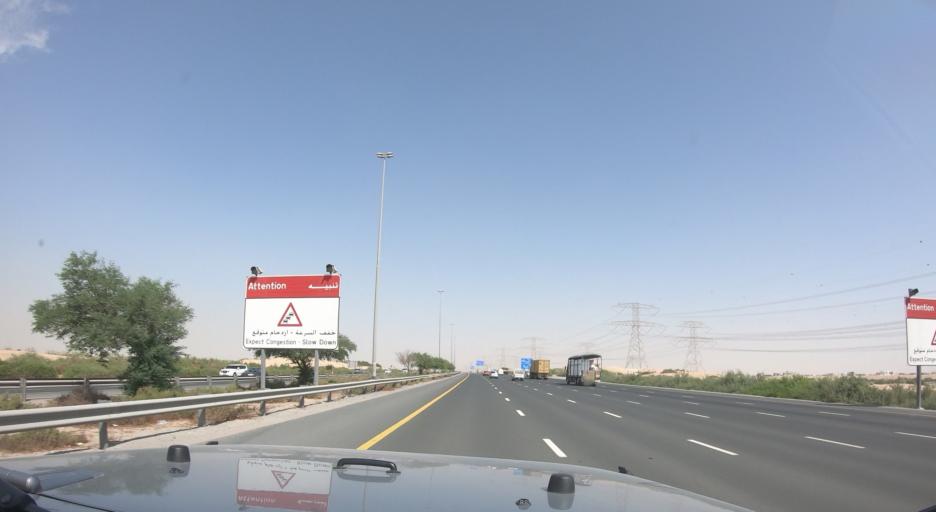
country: AE
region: Ash Shariqah
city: Sharjah
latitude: 25.2007
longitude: 55.5440
